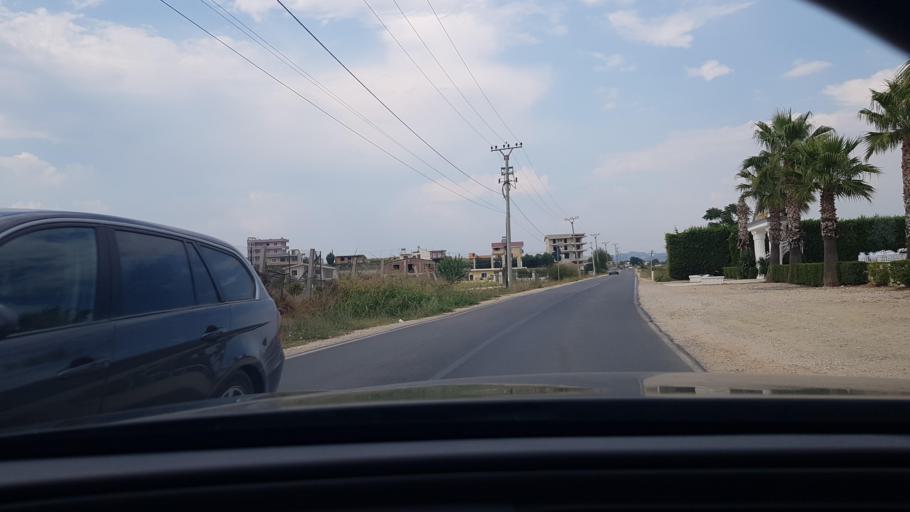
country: AL
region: Durres
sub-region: Rrethi i Durresit
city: Katundi i Ri
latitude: 41.4151
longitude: 19.5457
